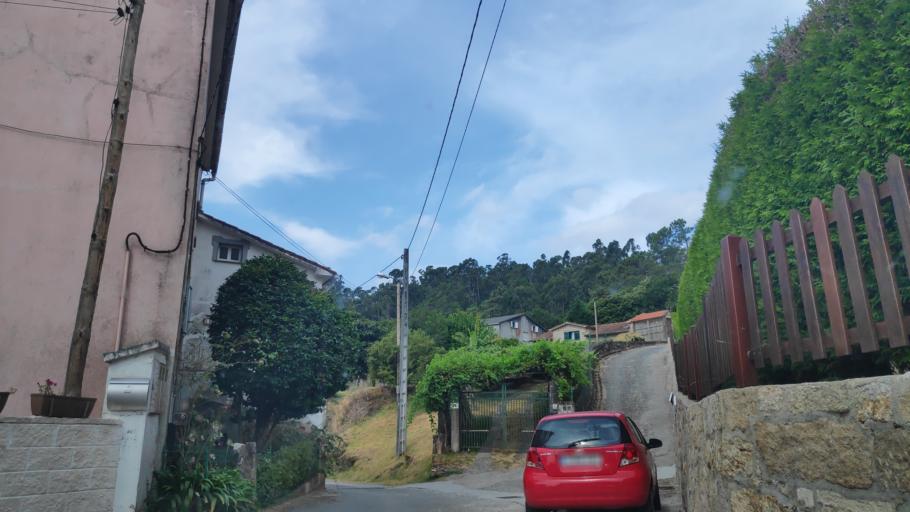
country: ES
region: Galicia
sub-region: Provincia da Coruna
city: Padron
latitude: 42.7304
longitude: -8.6731
